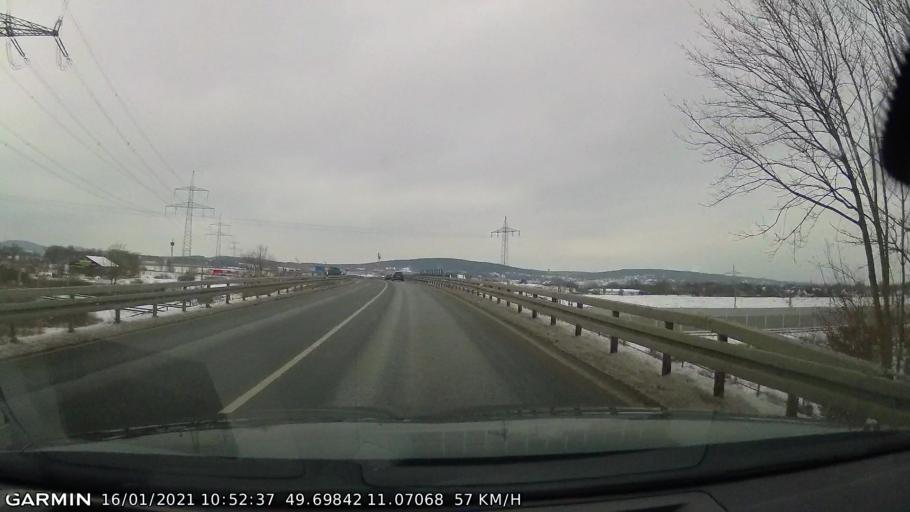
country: DE
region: Bavaria
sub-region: Upper Franconia
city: Forchheim
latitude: 49.6977
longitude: 11.0699
